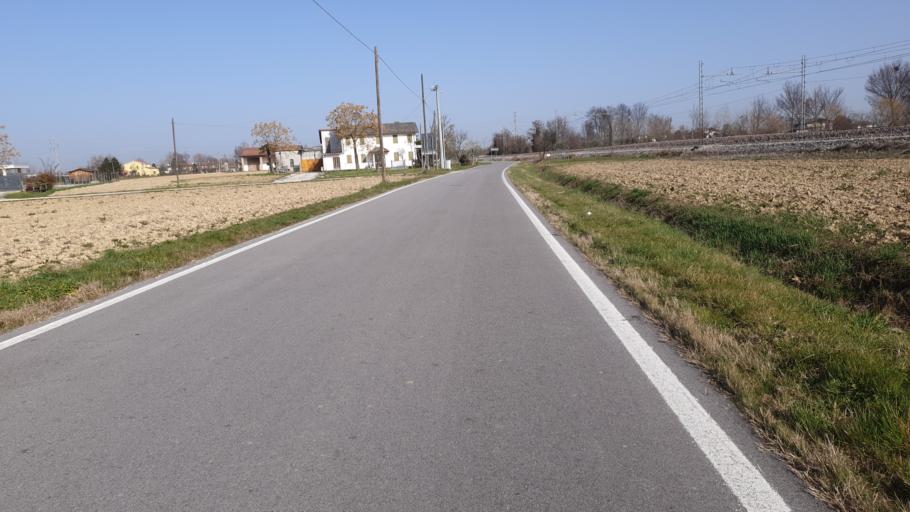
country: IT
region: Veneto
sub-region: Provincia di Padova
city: Campodarsego
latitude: 45.4890
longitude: 11.8963
